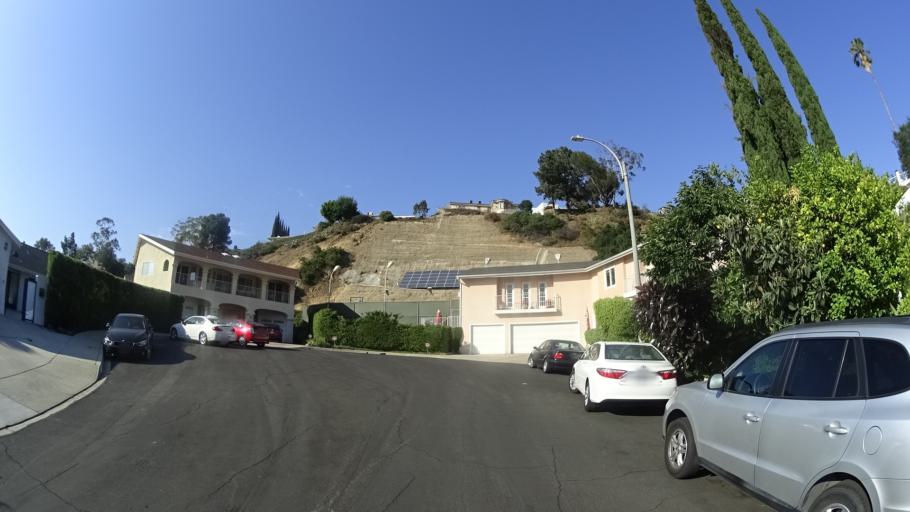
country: US
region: California
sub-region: Los Angeles County
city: Universal City
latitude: 34.1281
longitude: -118.3840
